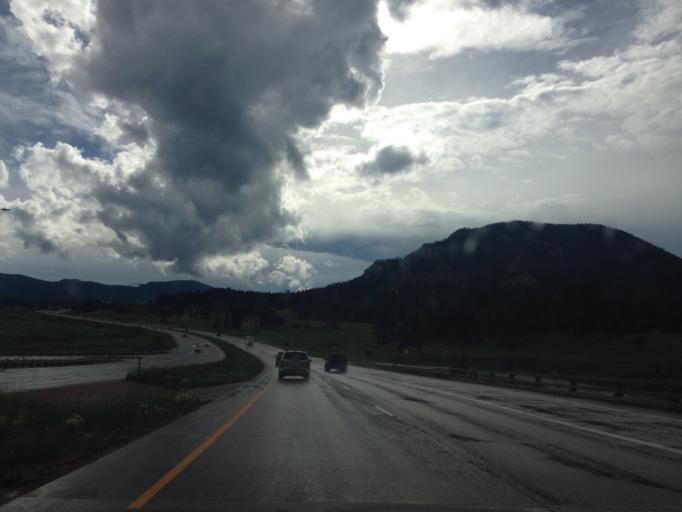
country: US
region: Colorado
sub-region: Jefferson County
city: Indian Hills
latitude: 39.5466
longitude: -105.2718
